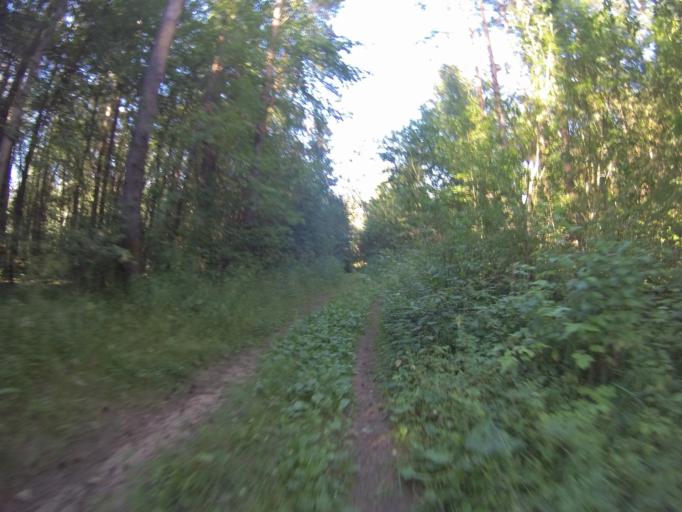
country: RU
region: Vladimir
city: Bogolyubovo
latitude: 56.1253
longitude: 40.5200
